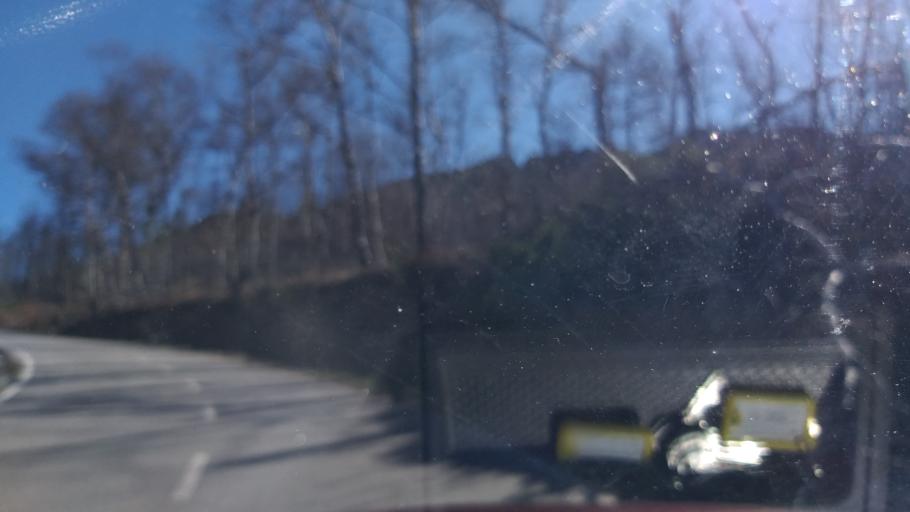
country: PT
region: Guarda
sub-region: Manteigas
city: Manteigas
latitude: 40.4880
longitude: -7.5232
